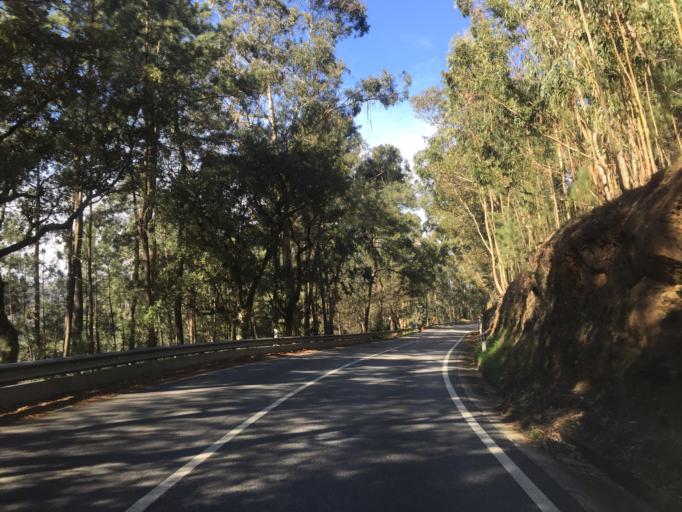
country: PT
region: Aveiro
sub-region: Vale de Cambra
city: Macieira de Cambra
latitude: 40.8985
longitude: -8.3302
